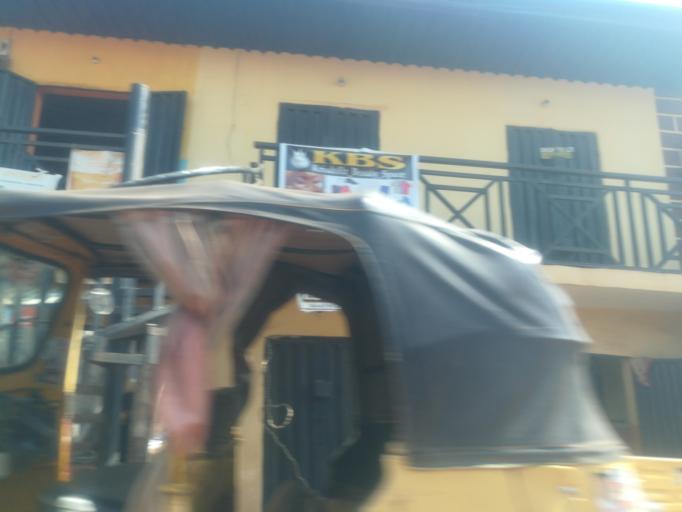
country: NG
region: Oyo
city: Egbeda
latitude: 7.4168
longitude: 3.9897
